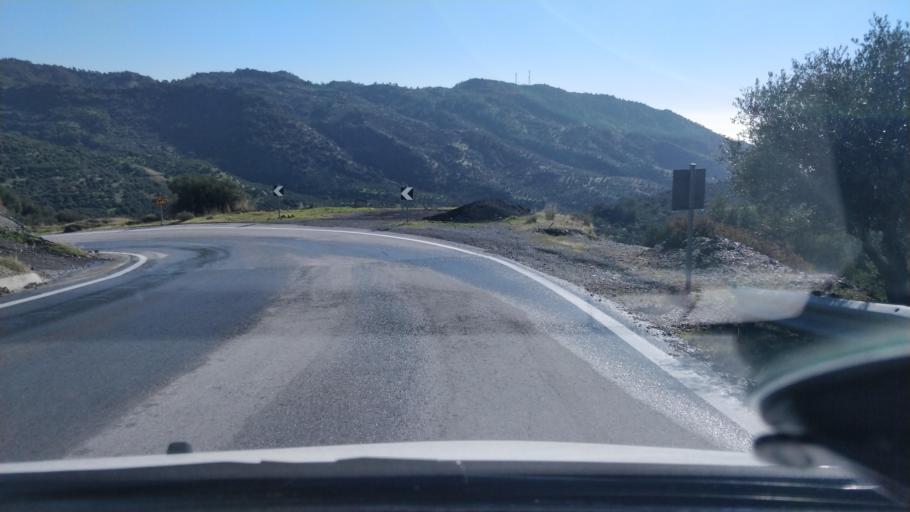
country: GR
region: Crete
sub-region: Nomos Irakleiou
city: Kastelli
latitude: 35.0334
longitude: 25.4458
